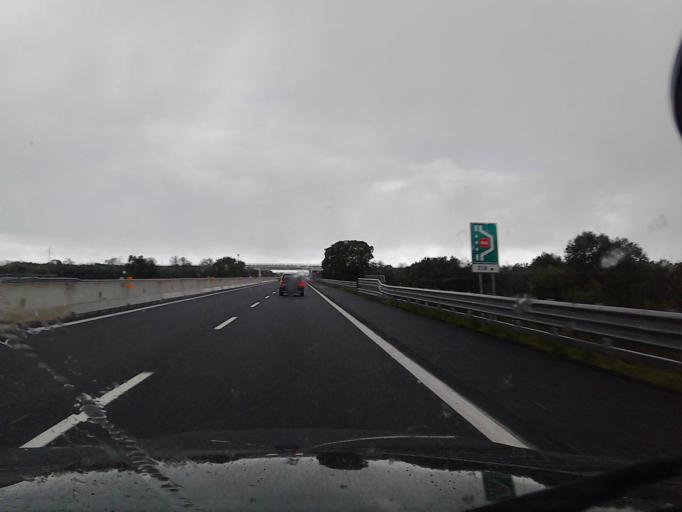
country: IT
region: Apulia
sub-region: Provincia di Bari
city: Giovinazzo
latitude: 41.1566
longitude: 16.6442
